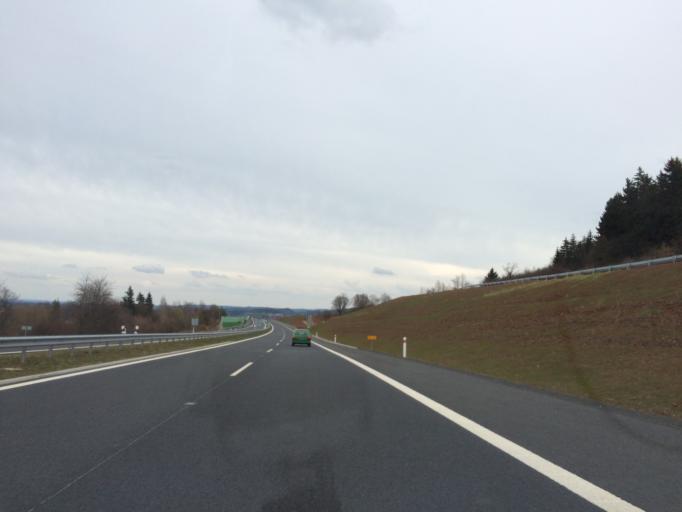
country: CZ
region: Ustecky
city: Lubenec
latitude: 50.1334
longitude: 13.2621
